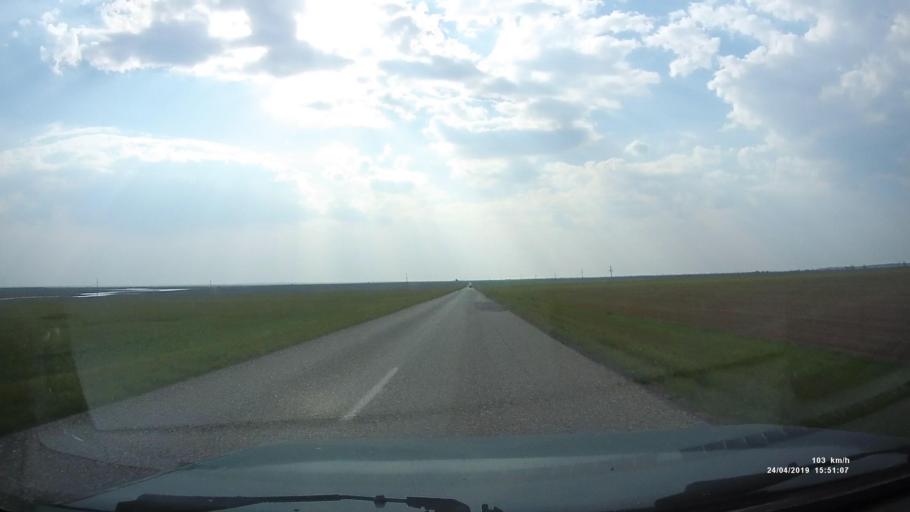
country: RU
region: Kalmykiya
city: Yashalta
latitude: 46.6043
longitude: 42.6180
